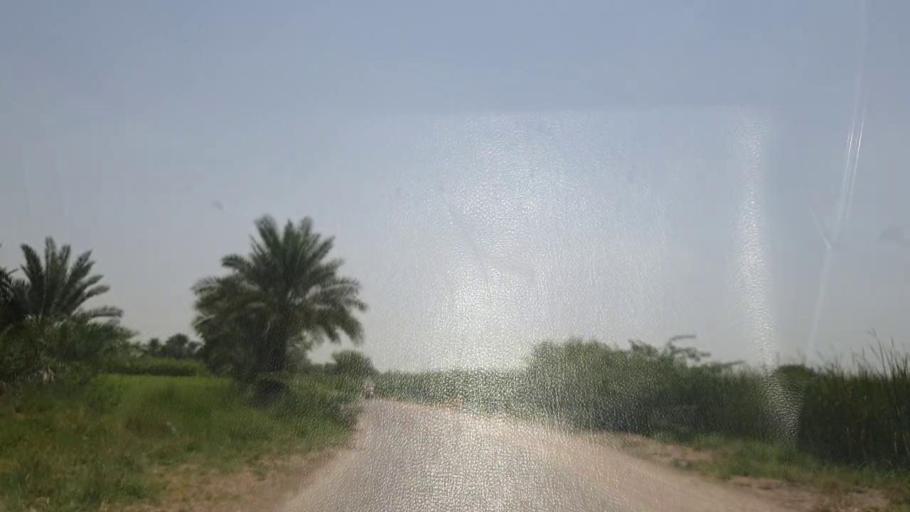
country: PK
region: Sindh
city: Bozdar
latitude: 27.2482
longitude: 68.6622
